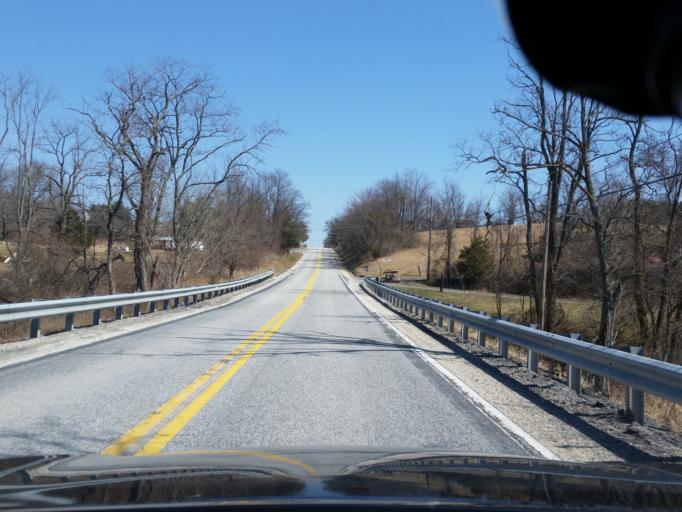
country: US
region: Pennsylvania
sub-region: Perry County
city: Duncannon
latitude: 40.3258
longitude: -77.0484
